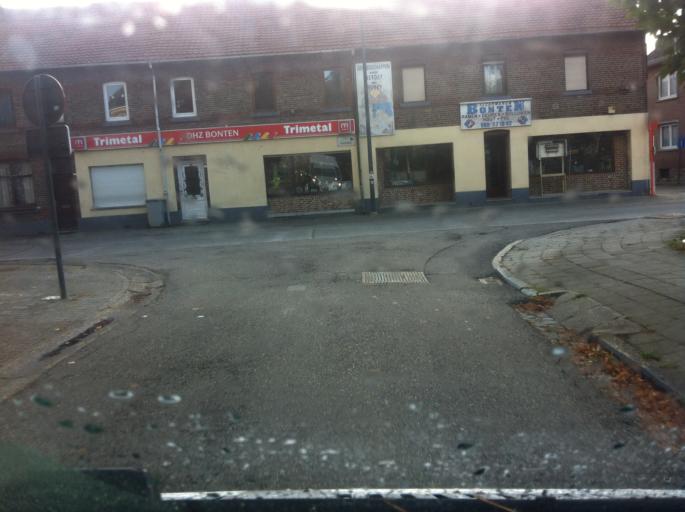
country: BE
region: Flanders
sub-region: Provincie Limburg
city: Maasmechelen
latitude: 50.9661
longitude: 5.6987
